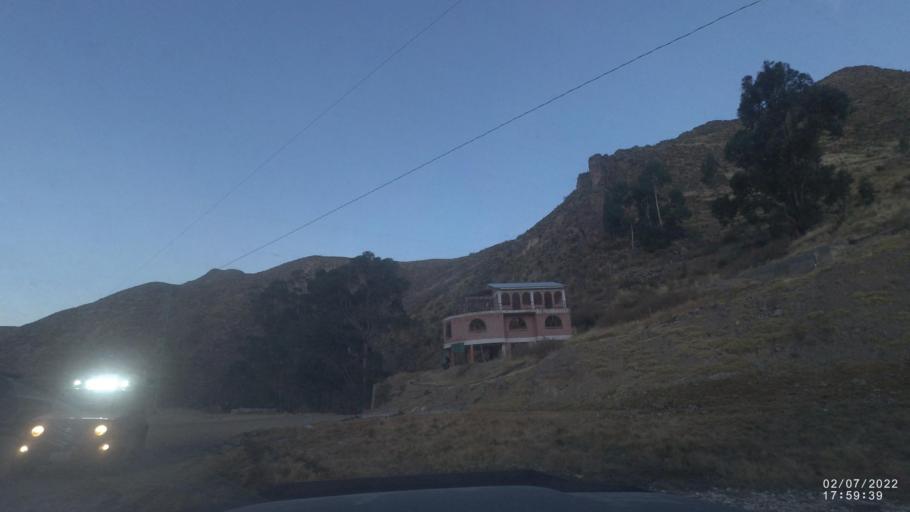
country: BO
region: Cochabamba
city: Irpa Irpa
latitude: -17.8413
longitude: -66.6159
